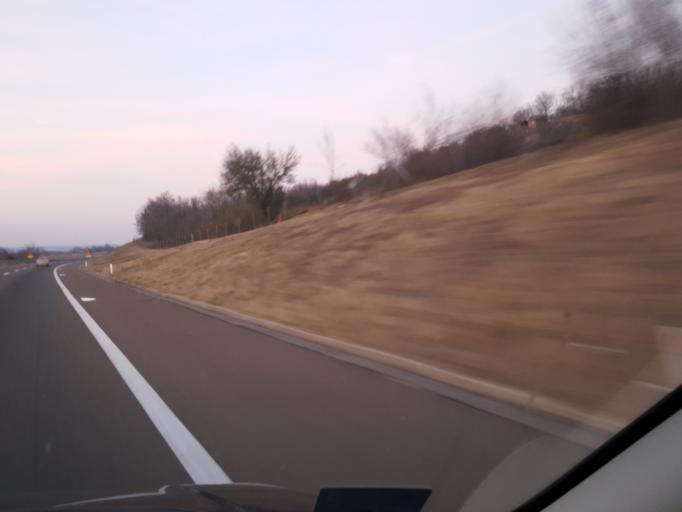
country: RS
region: Central Serbia
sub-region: Pomoravski Okrug
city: Paracin
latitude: 43.8336
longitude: 21.4278
